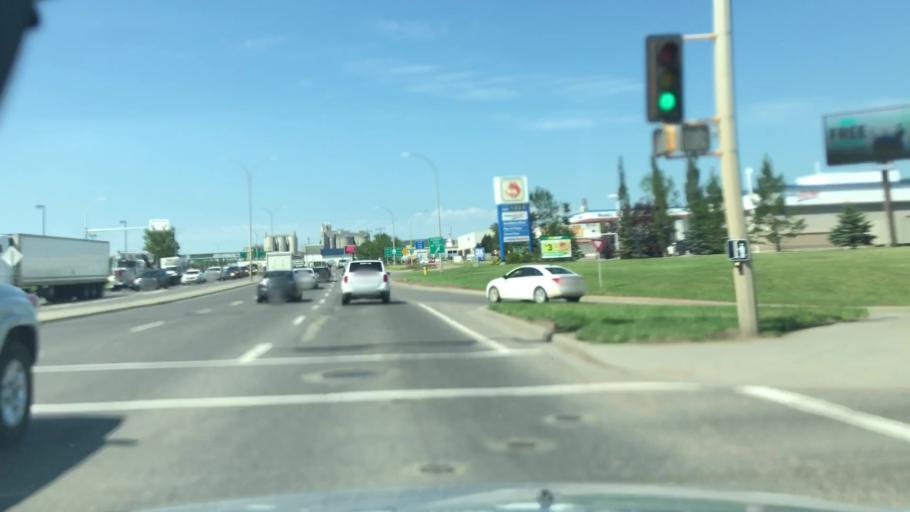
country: CA
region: Alberta
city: St. Albert
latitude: 53.5815
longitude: -113.5782
